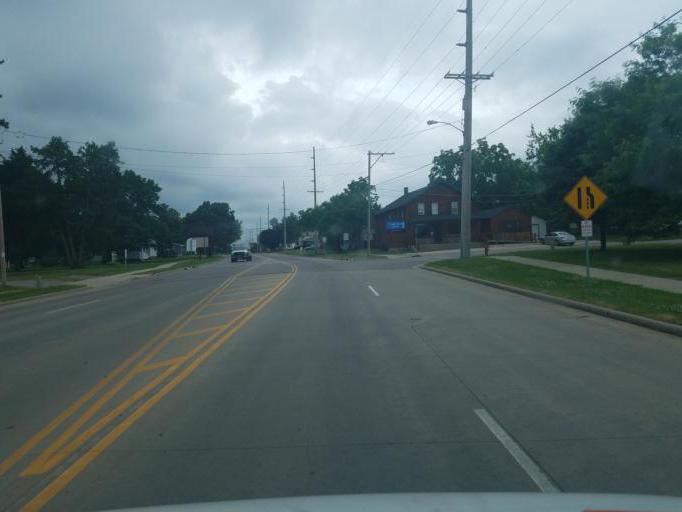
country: US
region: Wisconsin
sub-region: Juneau County
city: Mauston
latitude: 43.7987
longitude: -90.0700
